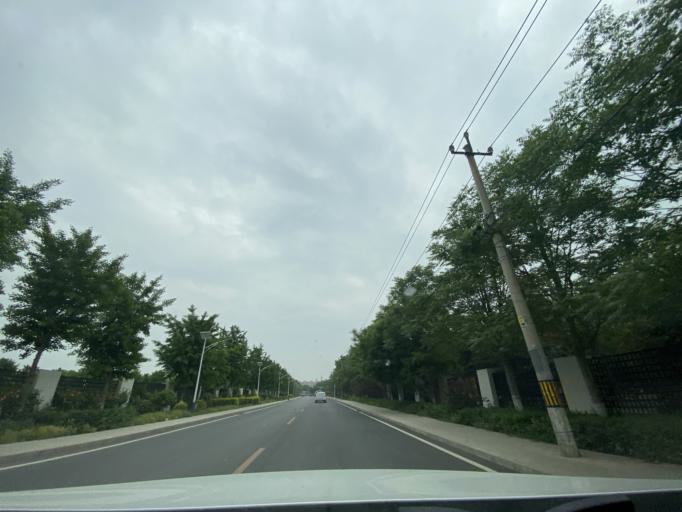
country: CN
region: Beijing
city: Sijiqing
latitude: 39.9373
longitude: 116.2392
